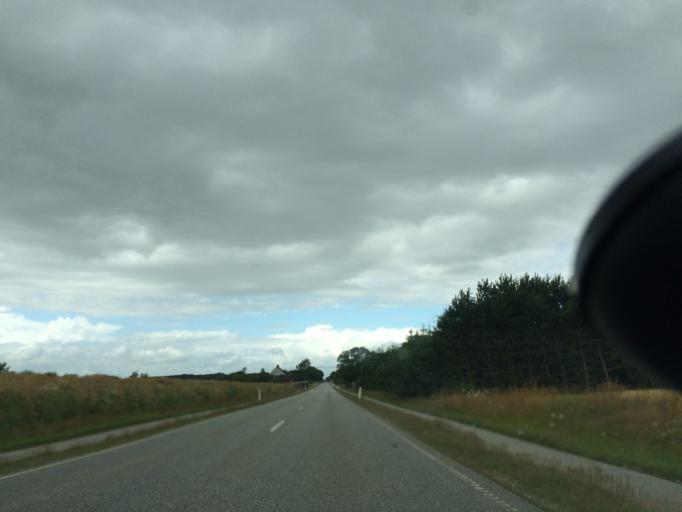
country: DK
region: Central Jutland
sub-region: Skanderborg Kommune
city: Galten
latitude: 56.1486
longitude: 9.8347
